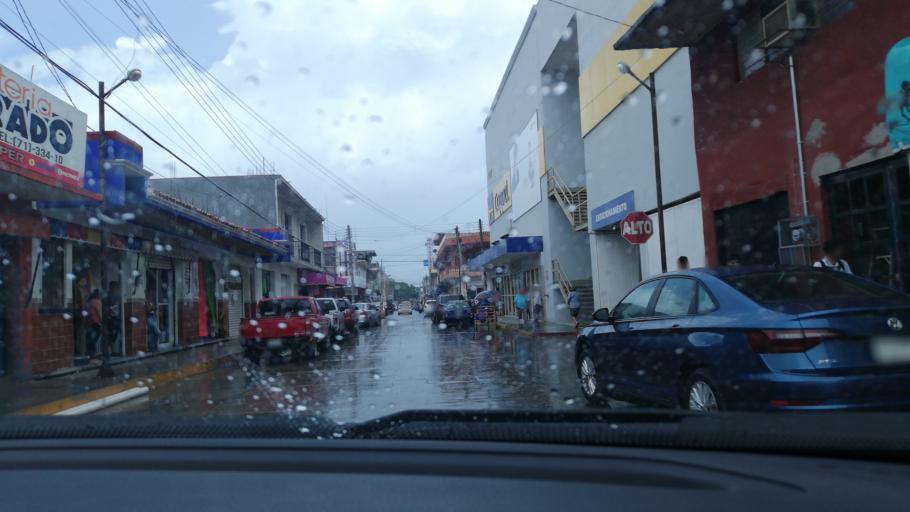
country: MX
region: Oaxaca
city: San Jeronimo Ixtepec
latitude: 16.5563
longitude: -95.0963
